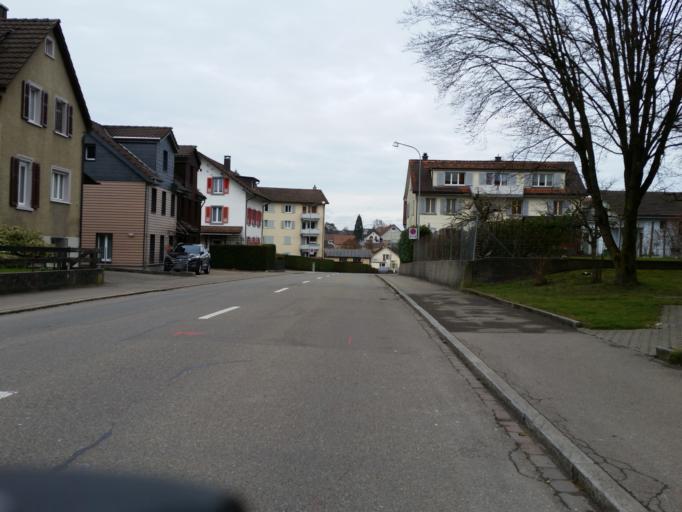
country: CH
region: Thurgau
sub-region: Arbon District
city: Amriswil
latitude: 47.5529
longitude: 9.3056
